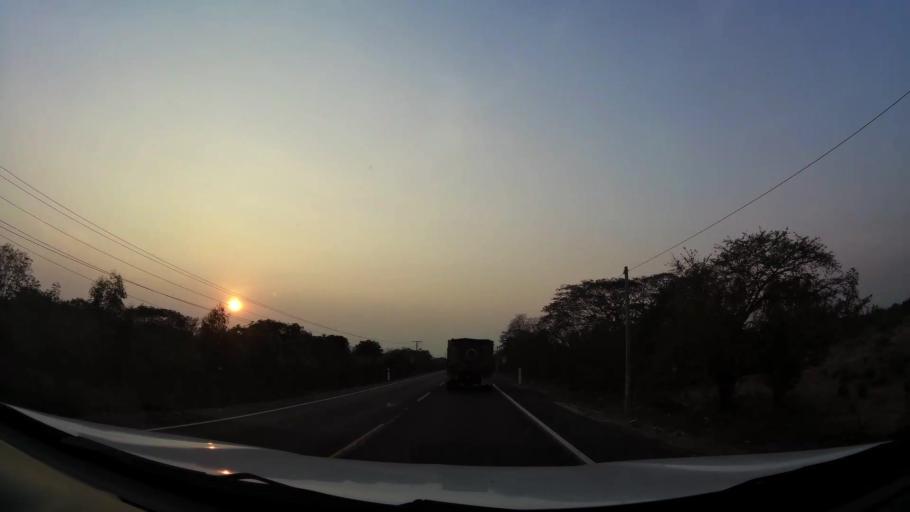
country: NI
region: Leon
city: La Paz Centro
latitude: 12.3113
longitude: -86.7844
